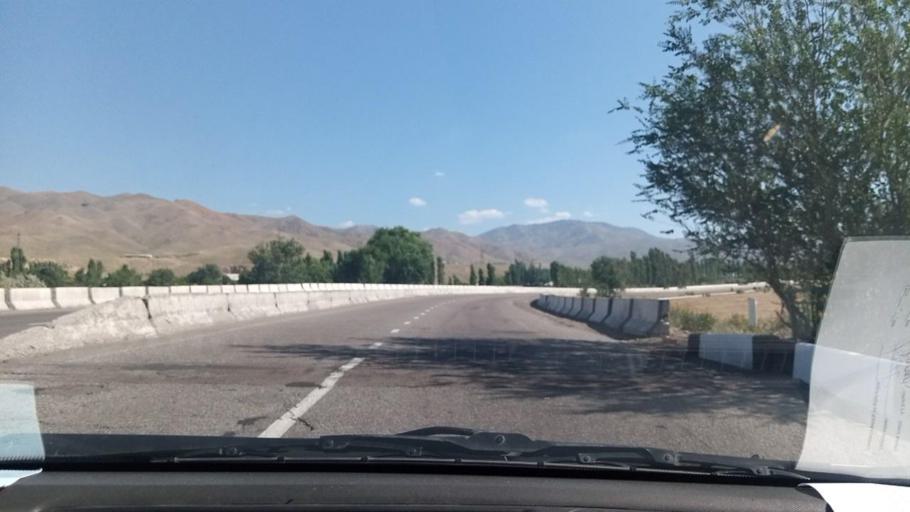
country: UZ
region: Toshkent
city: Angren
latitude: 40.9445
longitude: 69.9072
